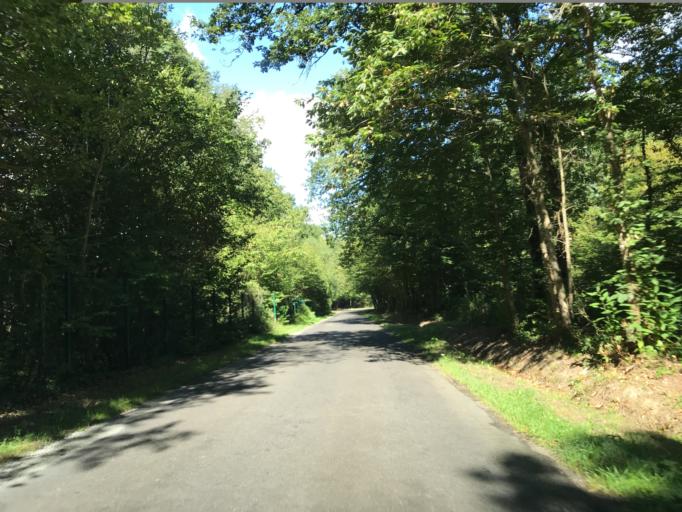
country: FR
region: Haute-Normandie
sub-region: Departement de l'Eure
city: La Chapelle-Reanville
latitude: 49.0838
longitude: 1.3954
